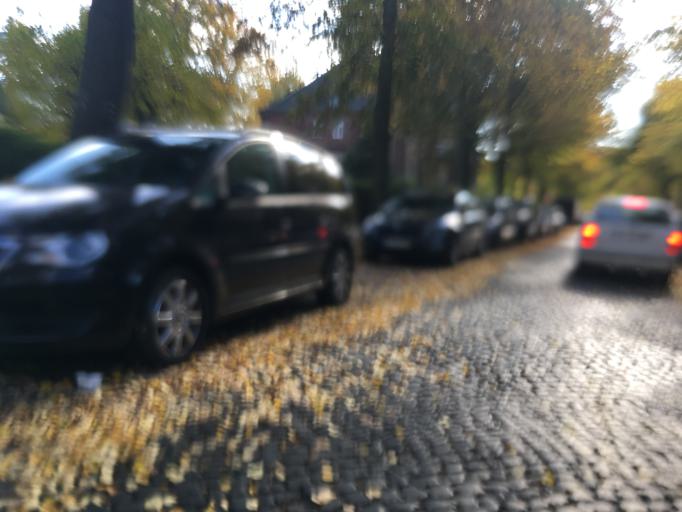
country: DE
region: Berlin
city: Wedding Bezirk
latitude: 52.5645
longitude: 13.3543
